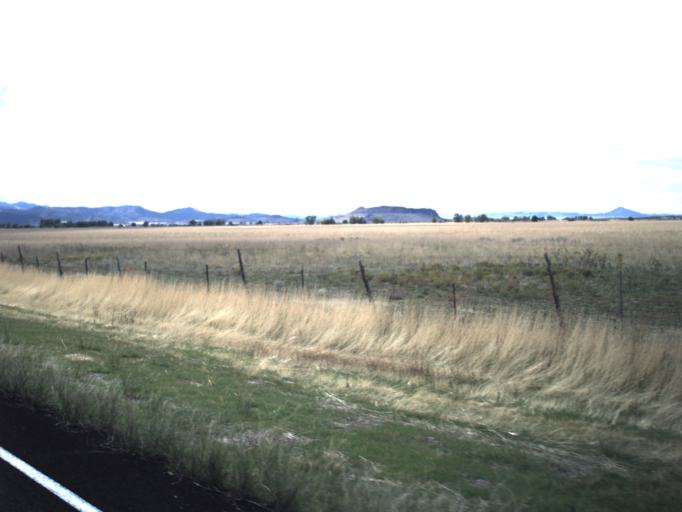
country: US
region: Utah
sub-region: Millard County
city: Fillmore
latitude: 38.8382
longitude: -112.4272
